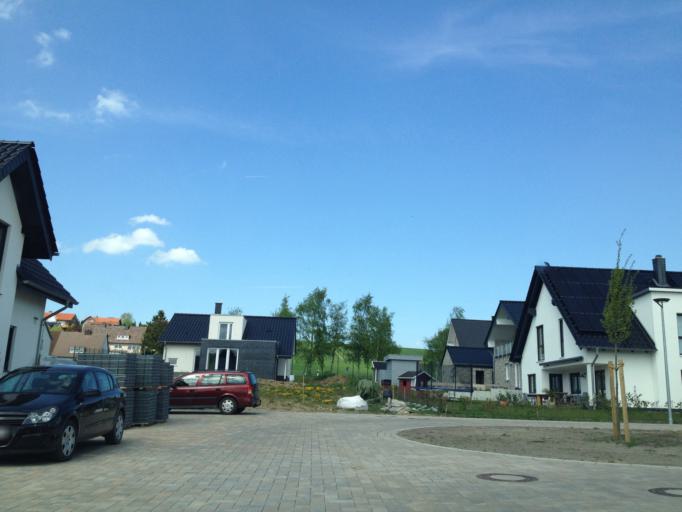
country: DE
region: North Rhine-Westphalia
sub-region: Regierungsbezirk Arnsberg
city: Mohnesee
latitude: 51.4982
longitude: 8.1399
